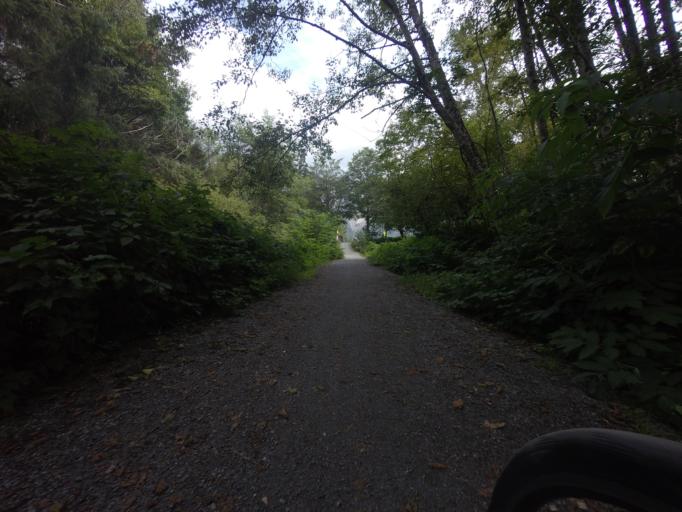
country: CA
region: British Columbia
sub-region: Greater Vancouver Regional District
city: Lions Bay
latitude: 49.7079
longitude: -123.1503
